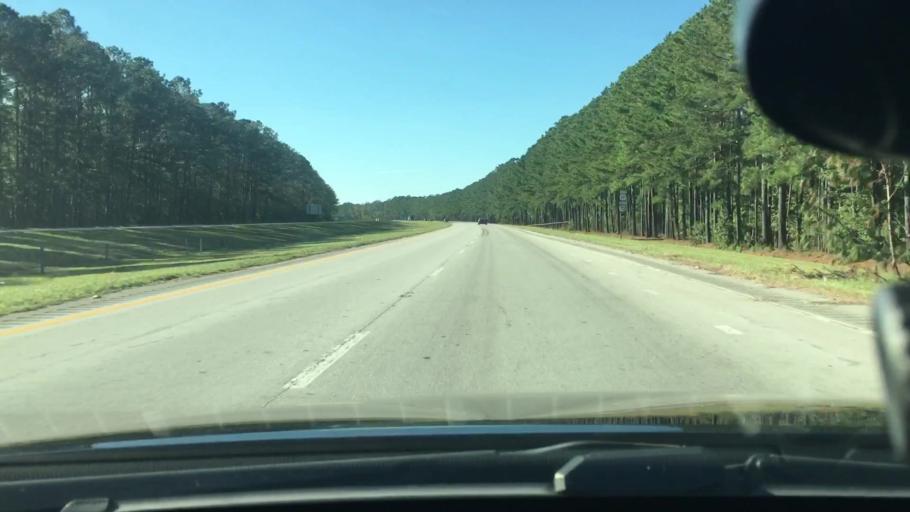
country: US
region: North Carolina
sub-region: Craven County
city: Trent Woods
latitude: 35.1166
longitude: -77.1032
